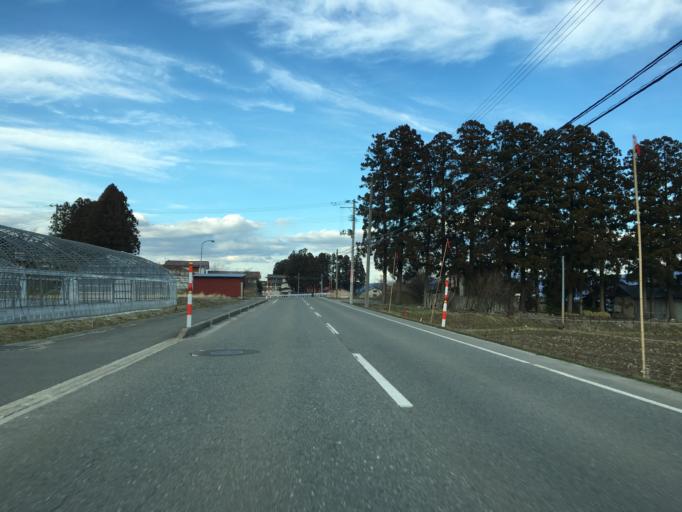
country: JP
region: Yamagata
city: Nagai
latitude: 38.1277
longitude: 140.0065
